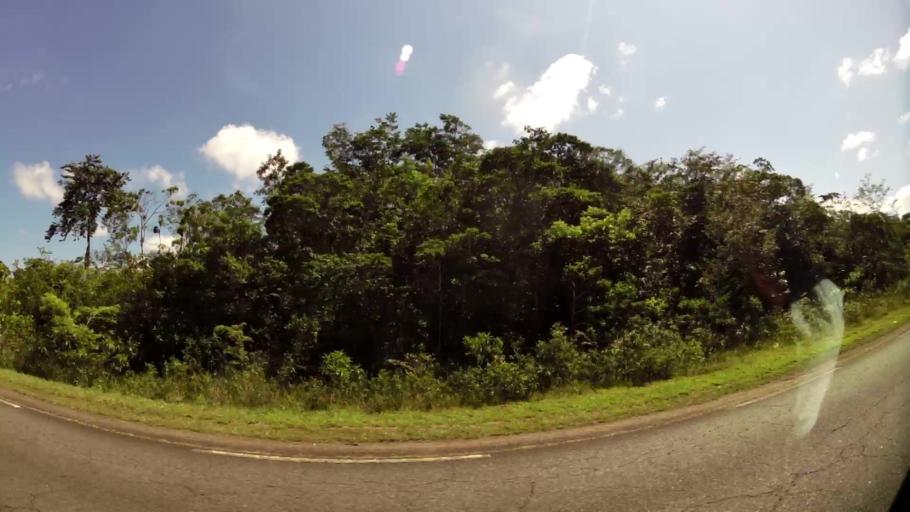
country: GF
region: Guyane
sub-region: Guyane
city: Matoury
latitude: 4.8346
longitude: -52.3306
